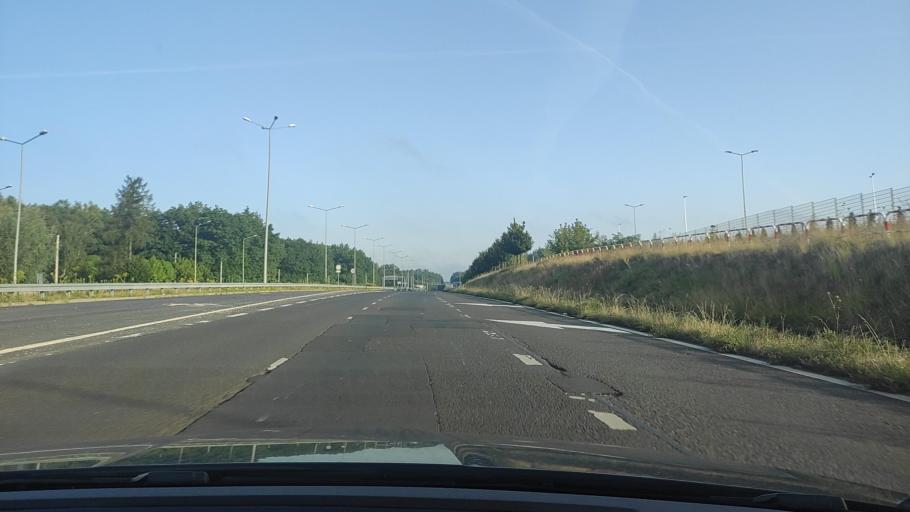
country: PL
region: Greater Poland Voivodeship
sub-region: Powiat poznanski
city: Swarzedz
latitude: 52.4126
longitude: 17.0254
